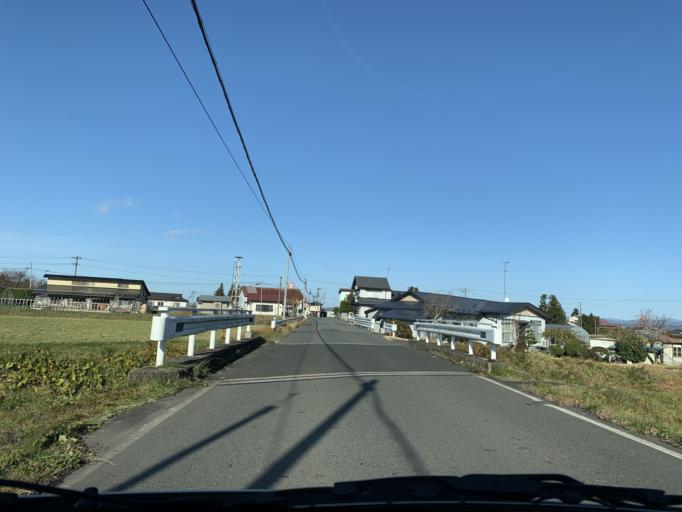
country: JP
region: Iwate
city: Mizusawa
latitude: 39.1593
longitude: 141.0981
